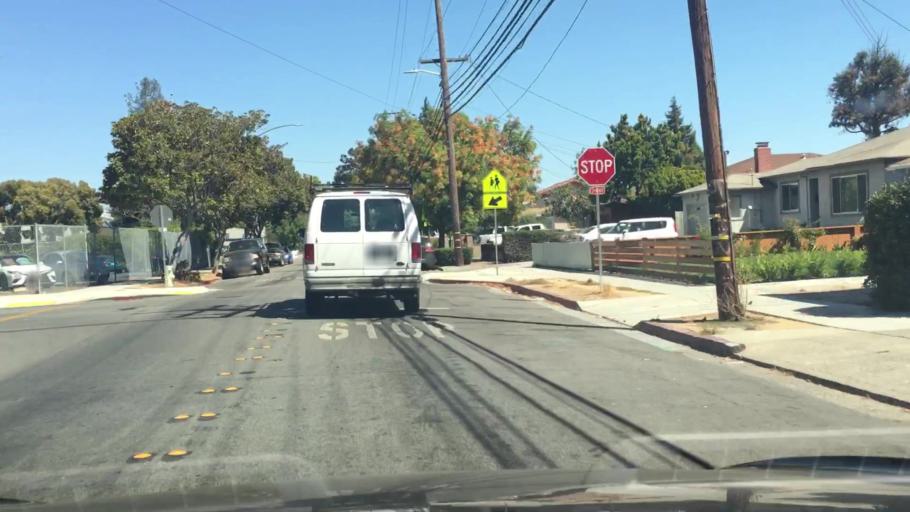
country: US
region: California
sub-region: San Mateo County
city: North Fair Oaks
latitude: 37.4804
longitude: -122.2154
